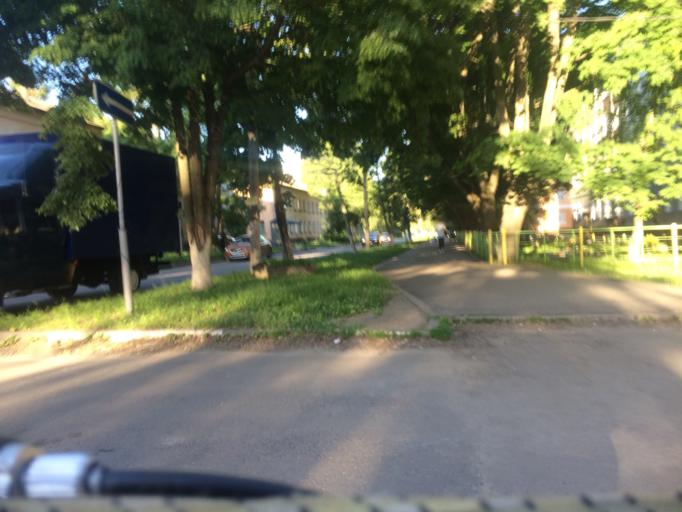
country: RU
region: Kursk
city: Kursk
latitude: 51.6744
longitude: 36.1517
